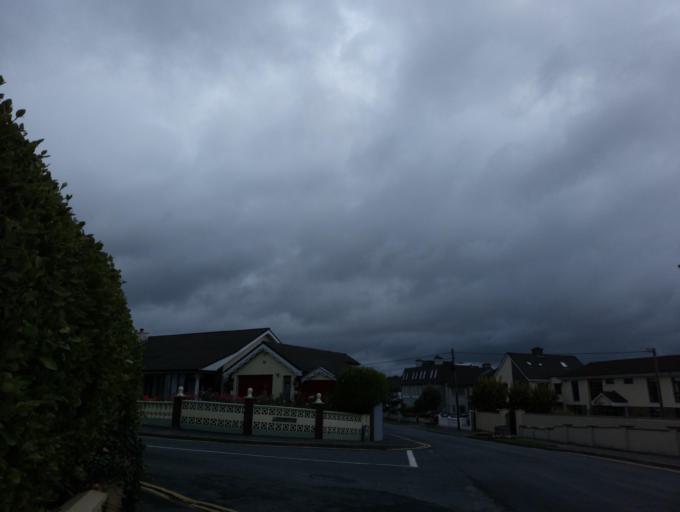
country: IE
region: Connaught
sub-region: County Galway
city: Gaillimh
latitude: 53.2616
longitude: -9.0783
